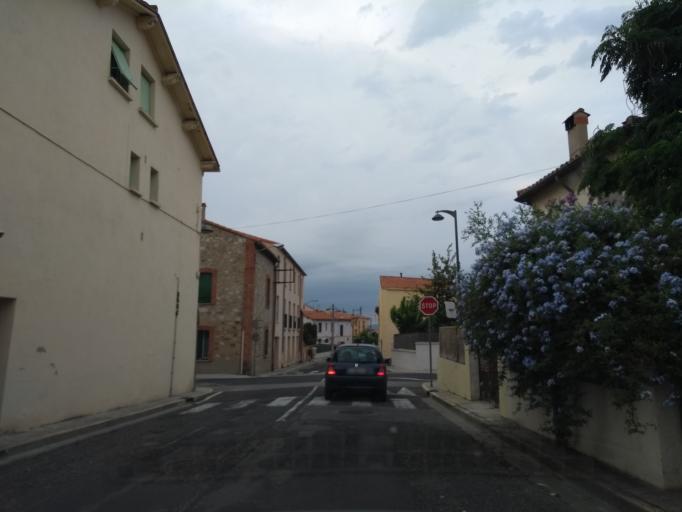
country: FR
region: Languedoc-Roussillon
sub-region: Departement des Pyrenees-Orientales
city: Elne
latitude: 42.6006
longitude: 2.9694
